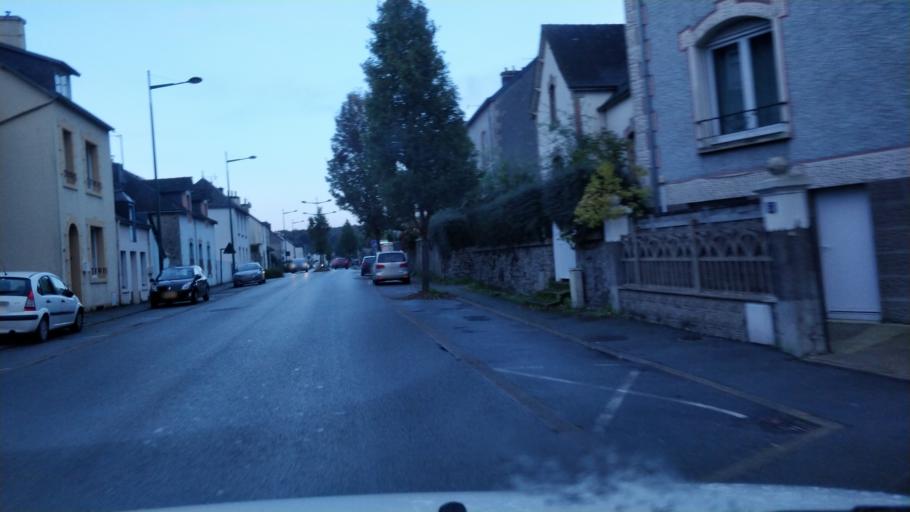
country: FR
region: Brittany
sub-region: Departement du Morbihan
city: Pontivy
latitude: 48.0741
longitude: -2.9617
